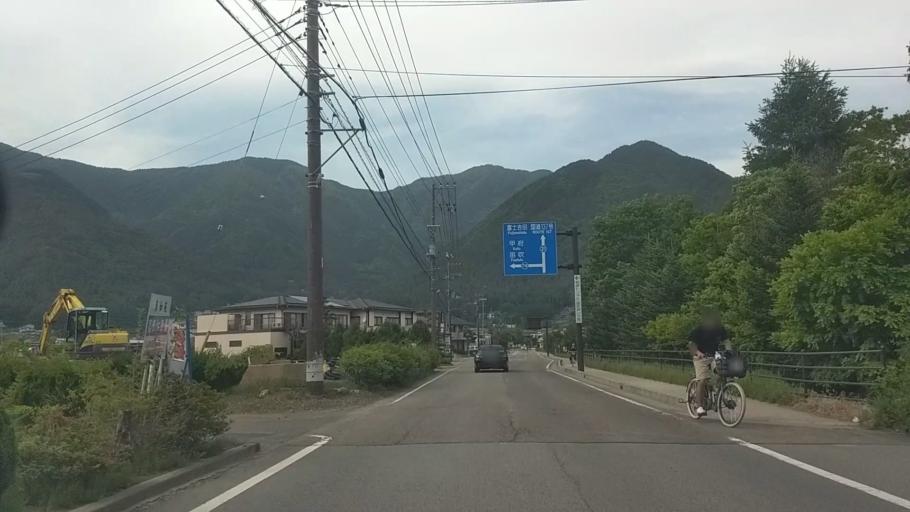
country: JP
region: Yamanashi
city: Fujikawaguchiko
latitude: 35.5195
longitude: 138.7408
